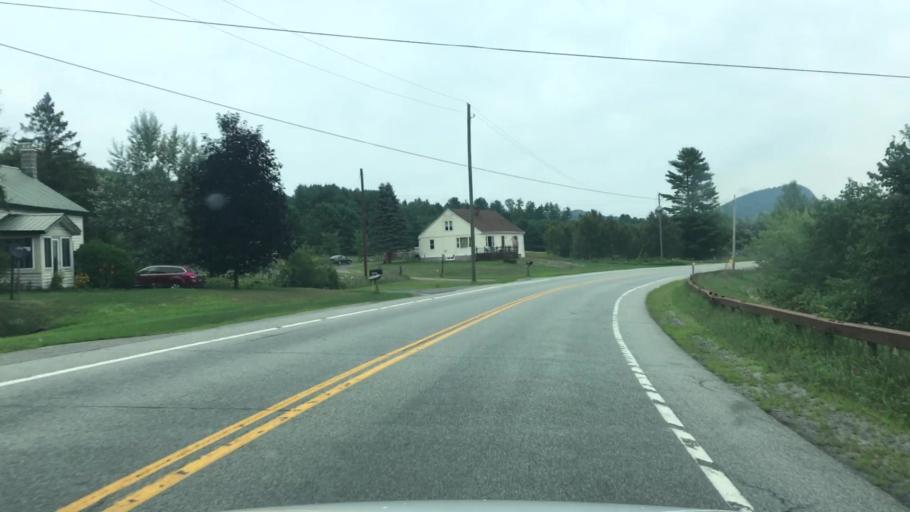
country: US
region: New York
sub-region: Essex County
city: Elizabethtown
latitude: 44.4053
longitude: -73.7025
